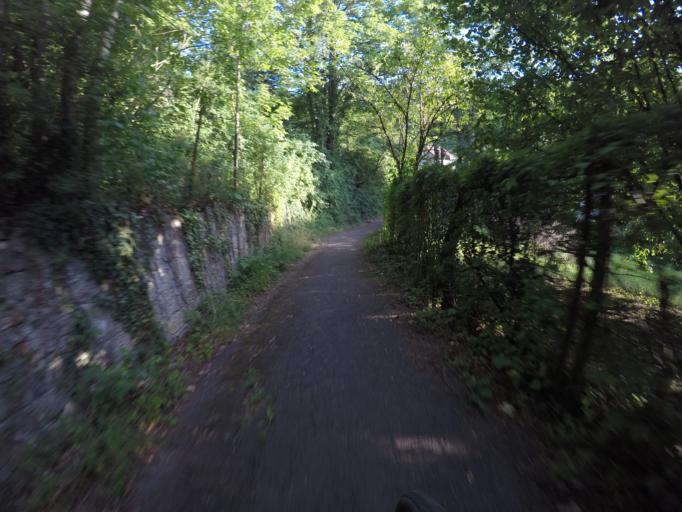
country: DE
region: Baden-Wuerttemberg
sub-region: Regierungsbezirk Stuttgart
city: Stuttgart-Ost
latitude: 48.7774
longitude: 9.2153
